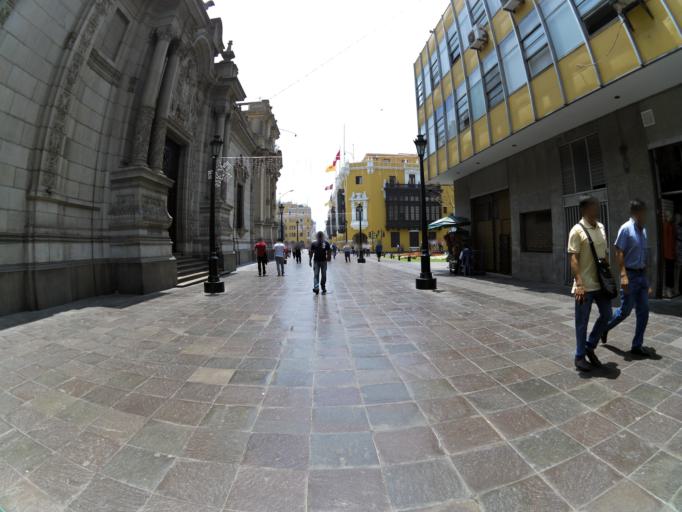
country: PE
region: Lima
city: Lima
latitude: -12.0447
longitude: -77.0304
